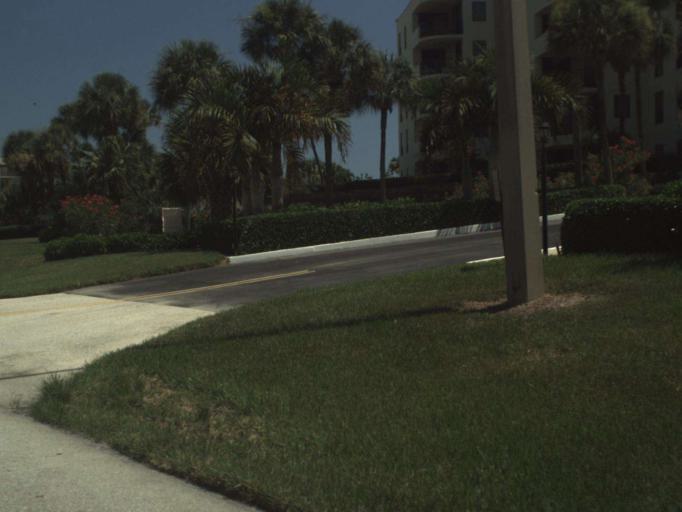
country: US
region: Florida
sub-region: Indian River County
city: Vero Beach
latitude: 27.6678
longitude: -80.3608
